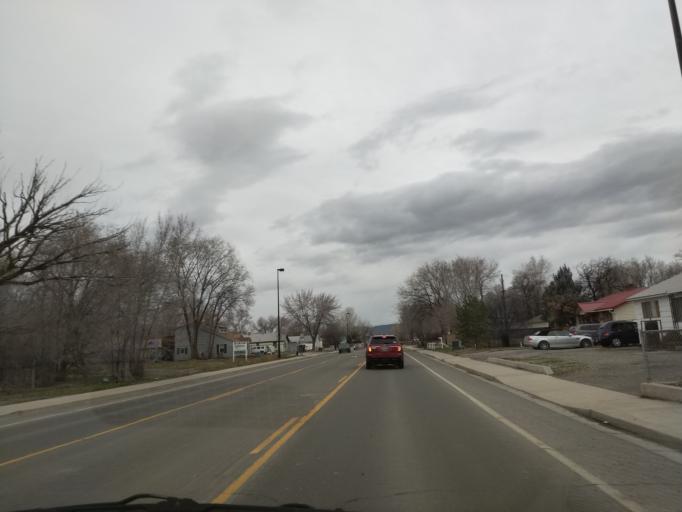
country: US
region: Colorado
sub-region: Mesa County
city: Fruitvale
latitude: 39.0817
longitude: -108.5152
